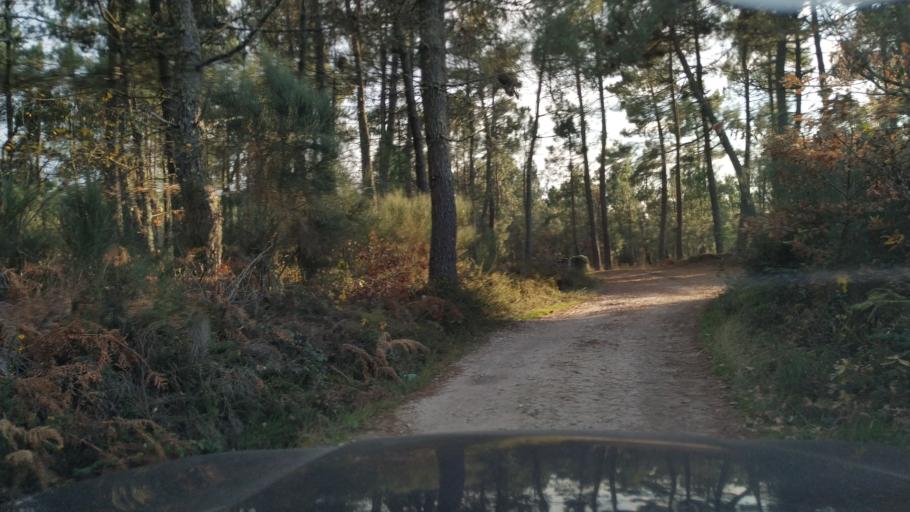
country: PT
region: Vila Real
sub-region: Sabrosa
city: Sabrosa
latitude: 41.3230
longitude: -7.6227
